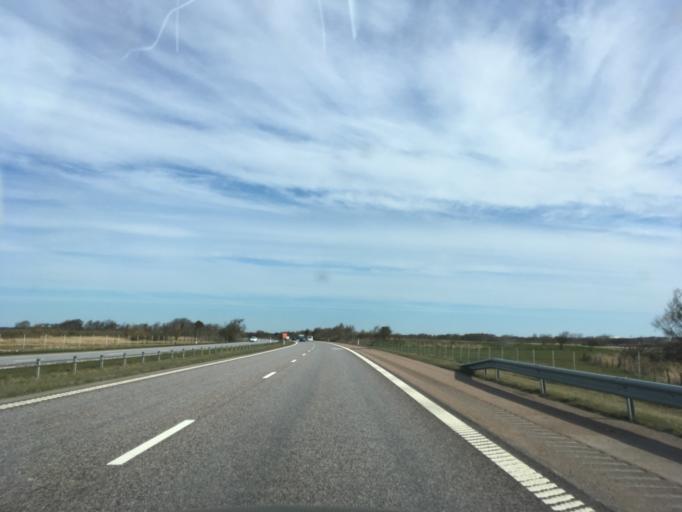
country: SE
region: Halland
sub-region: Halmstads Kommun
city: Troenninge
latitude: 56.6233
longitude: 12.9158
